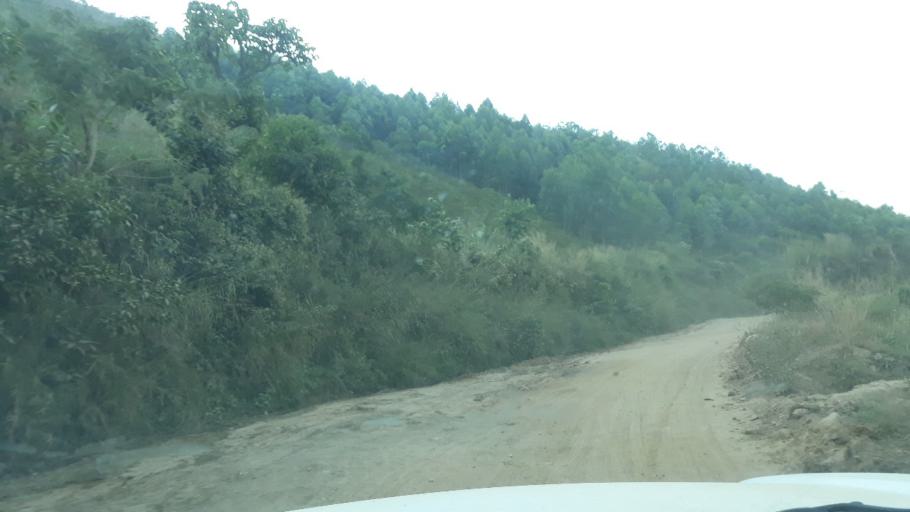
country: RW
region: Western Province
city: Cyangugu
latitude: -2.7033
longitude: 28.9528
